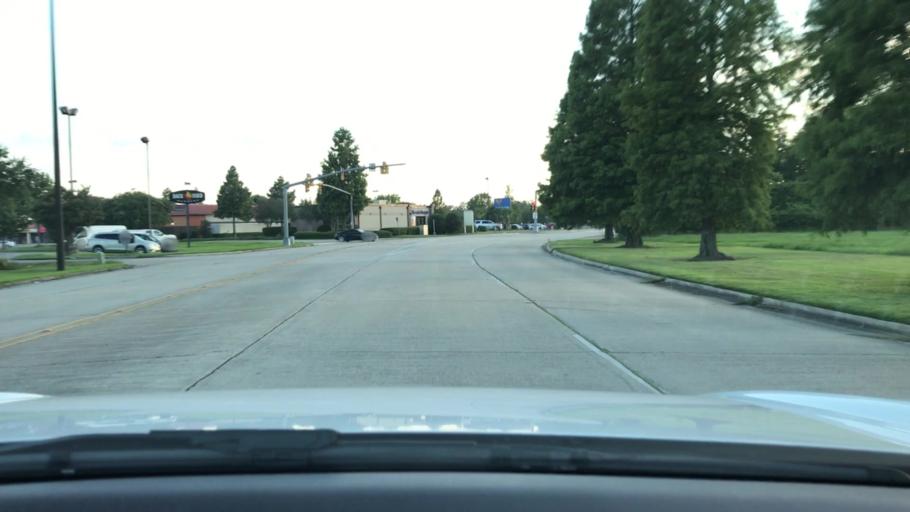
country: US
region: Louisiana
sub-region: East Baton Rouge Parish
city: Village Saint George
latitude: 30.3797
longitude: -91.0647
